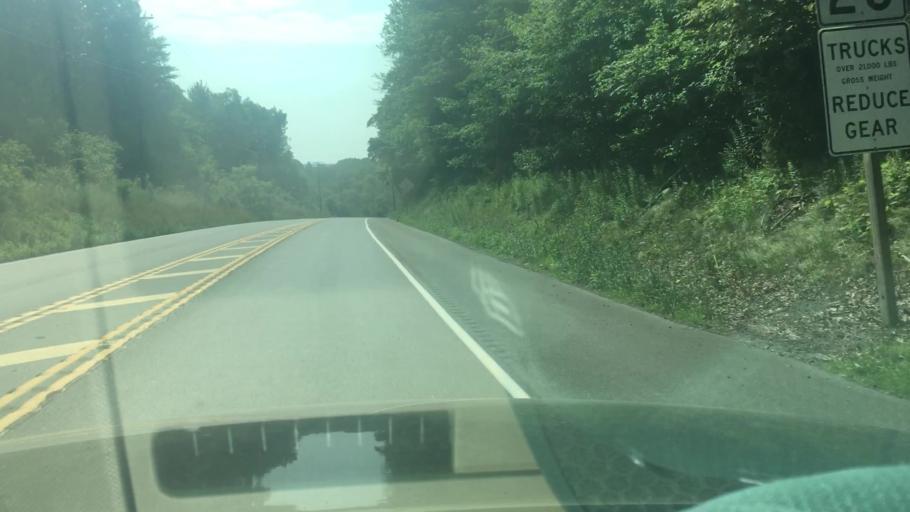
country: US
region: Pennsylvania
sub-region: Northumberland County
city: Kulpmont
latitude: 40.8150
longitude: -76.4563
